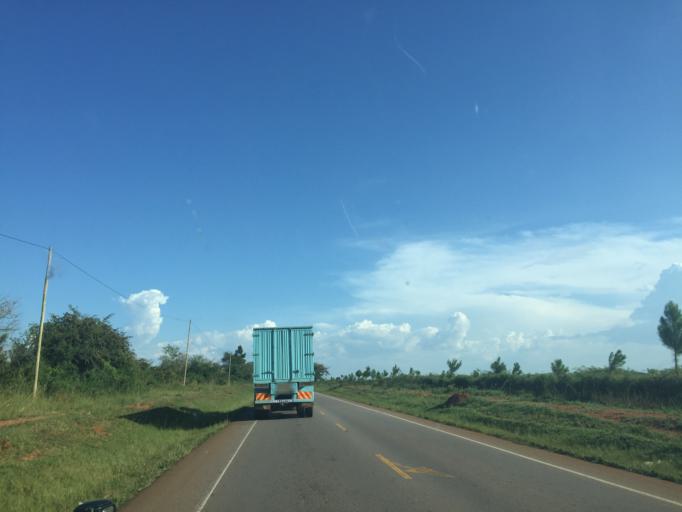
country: UG
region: Central Region
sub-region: Nakasongola District
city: Nakasongola
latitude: 1.2949
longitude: 32.4245
